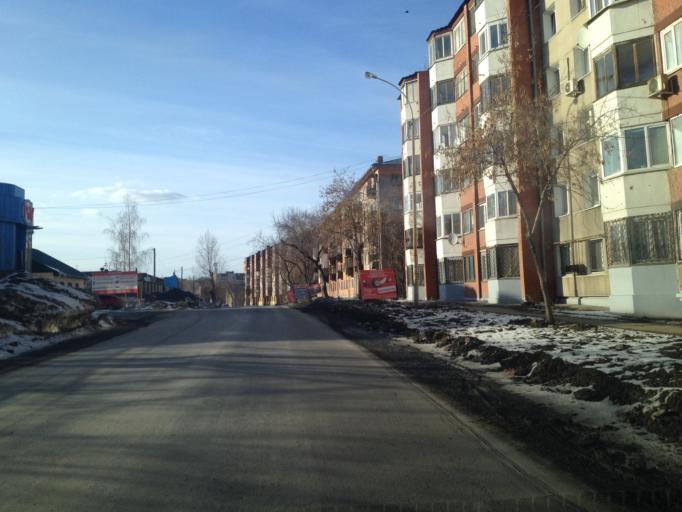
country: RU
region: Sverdlovsk
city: Shuvakish
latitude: 56.8657
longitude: 60.5275
